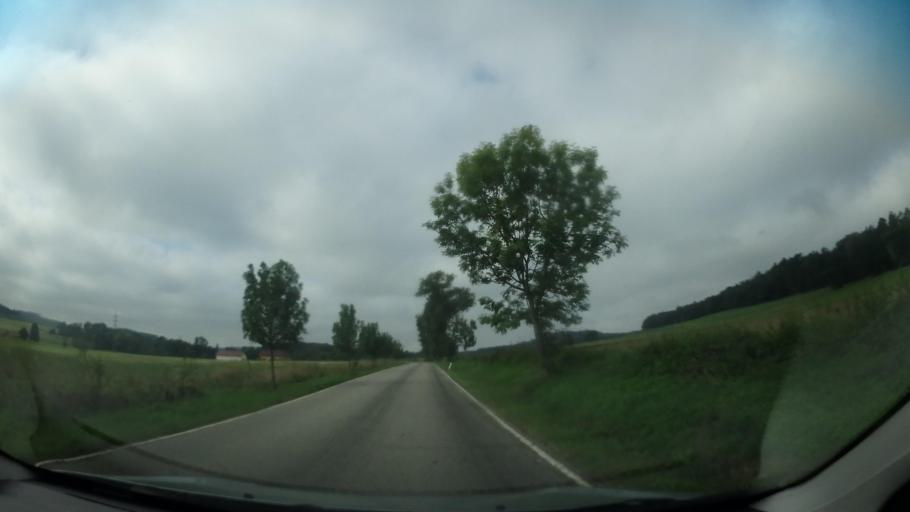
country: CZ
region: Central Bohemia
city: Neveklov
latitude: 49.7502
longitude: 14.5226
